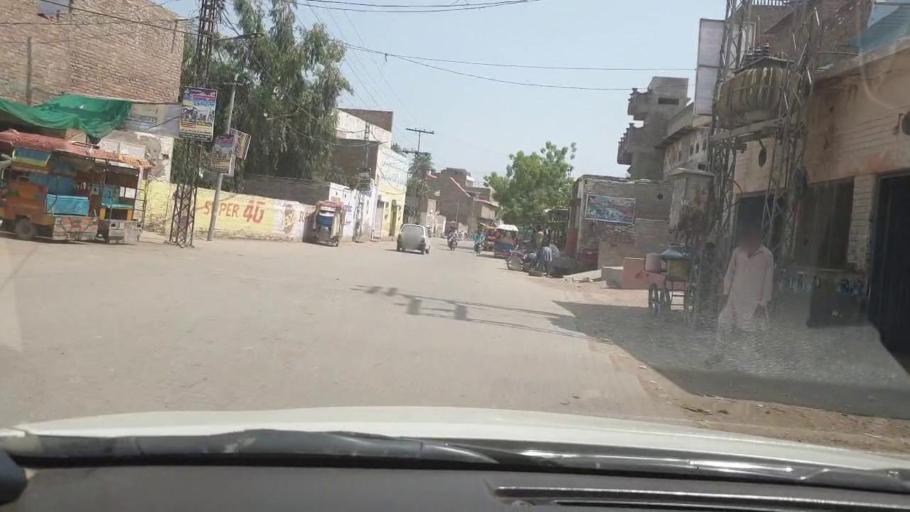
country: PK
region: Sindh
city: Shikarpur
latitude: 27.9530
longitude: 68.6284
